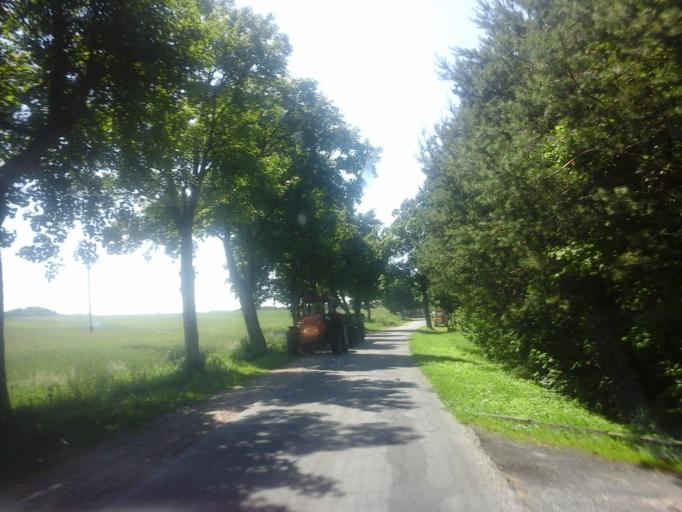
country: PL
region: West Pomeranian Voivodeship
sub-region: Powiat bialogardzki
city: Bialogard
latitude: 54.0751
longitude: 16.0443
